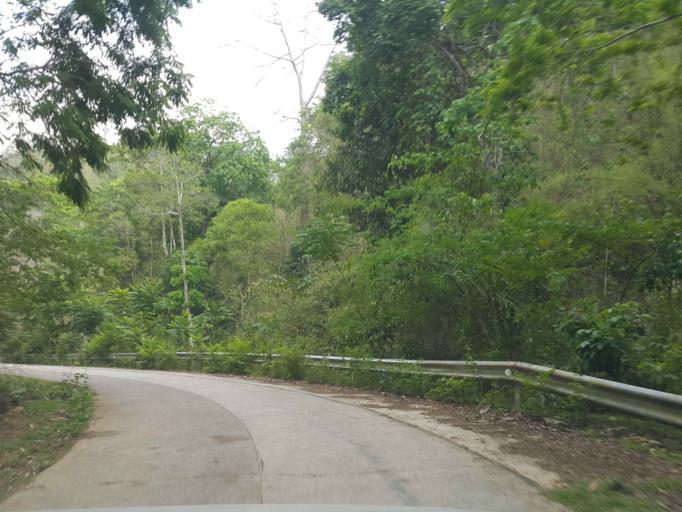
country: TH
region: Chiang Mai
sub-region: Amphoe Chiang Dao
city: Chiang Dao
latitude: 19.3750
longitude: 98.7548
